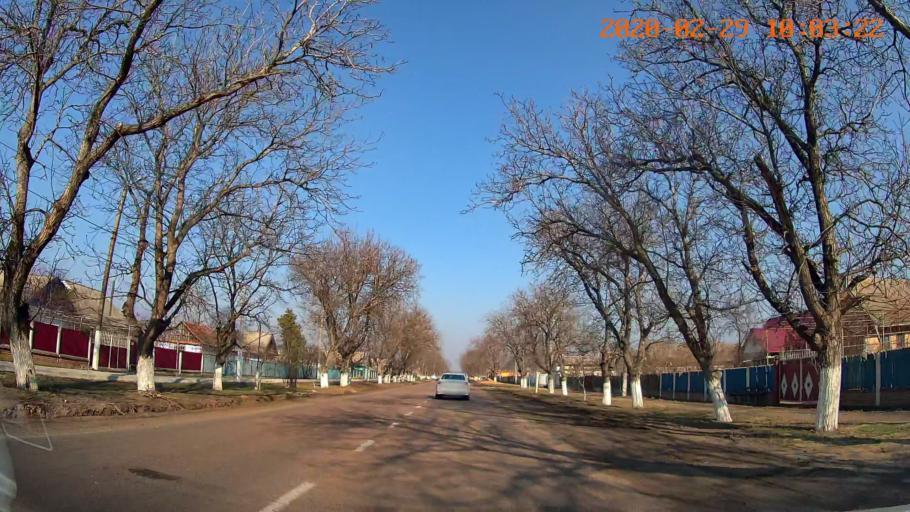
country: MD
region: Causeni
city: Chitcani
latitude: 46.7901
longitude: 29.6805
